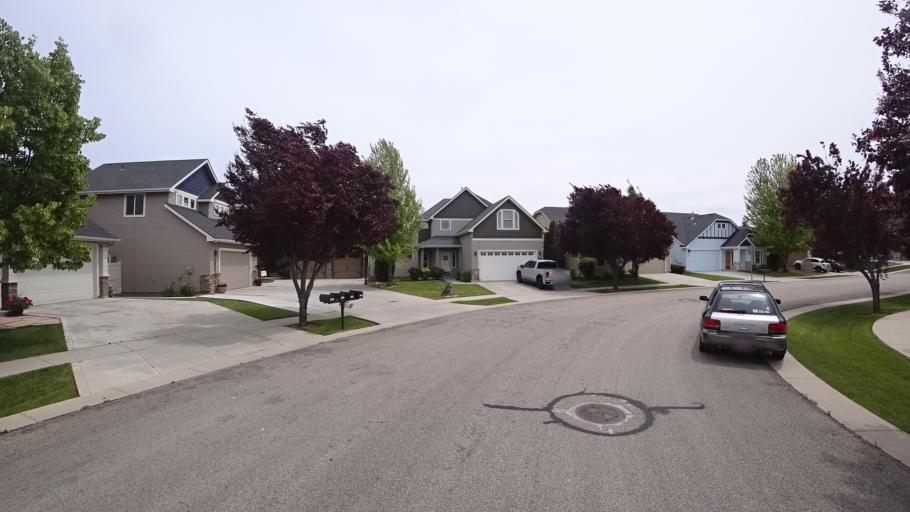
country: US
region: Idaho
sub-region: Ada County
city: Meridian
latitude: 43.5764
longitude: -116.3720
